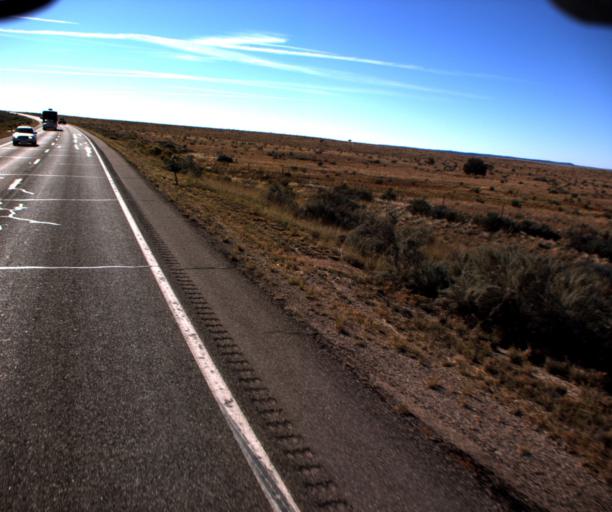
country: US
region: Arizona
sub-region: Mohave County
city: Colorado City
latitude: 36.8936
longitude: -112.9138
